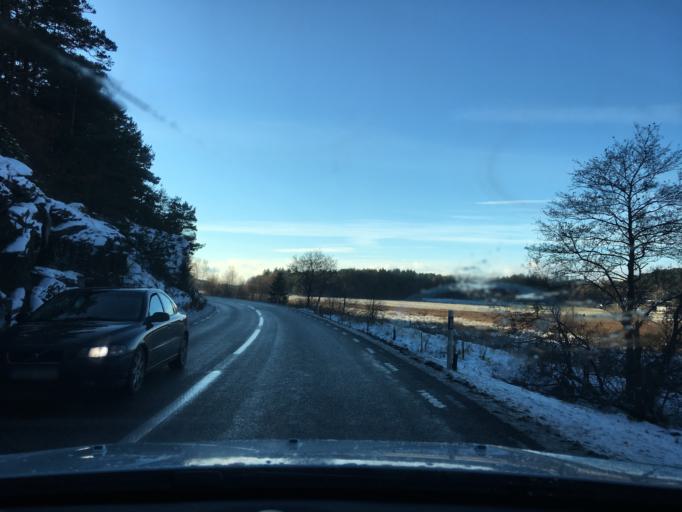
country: SE
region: Vaestra Goetaland
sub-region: Tjorns Kommun
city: Myggenas
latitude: 58.1165
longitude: 11.7062
